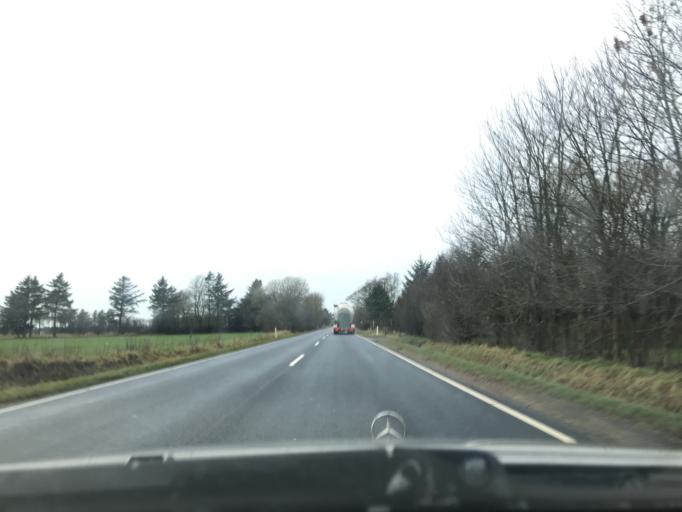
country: DK
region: South Denmark
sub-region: Esbjerg Kommune
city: Ribe
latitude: 55.2904
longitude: 8.8242
